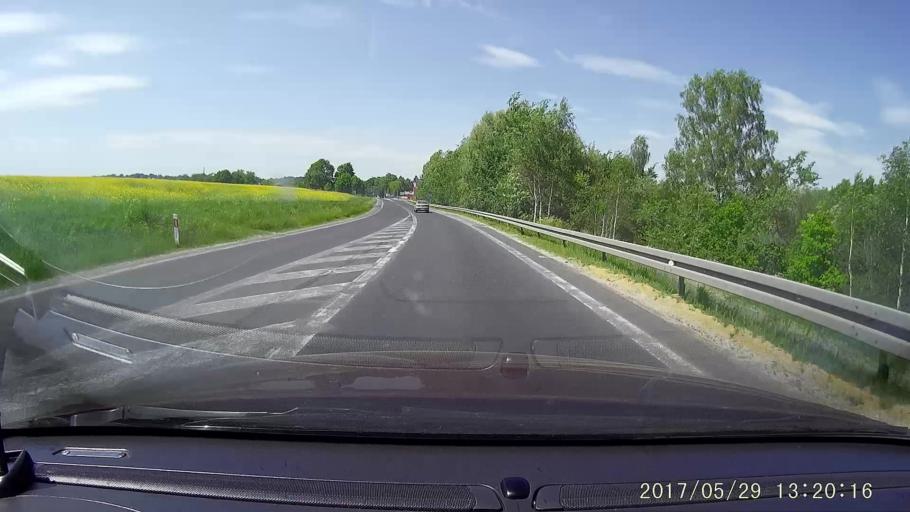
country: PL
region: Lower Silesian Voivodeship
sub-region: Powiat lwowecki
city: Gryfow Slaski
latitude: 51.0222
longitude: 15.4310
